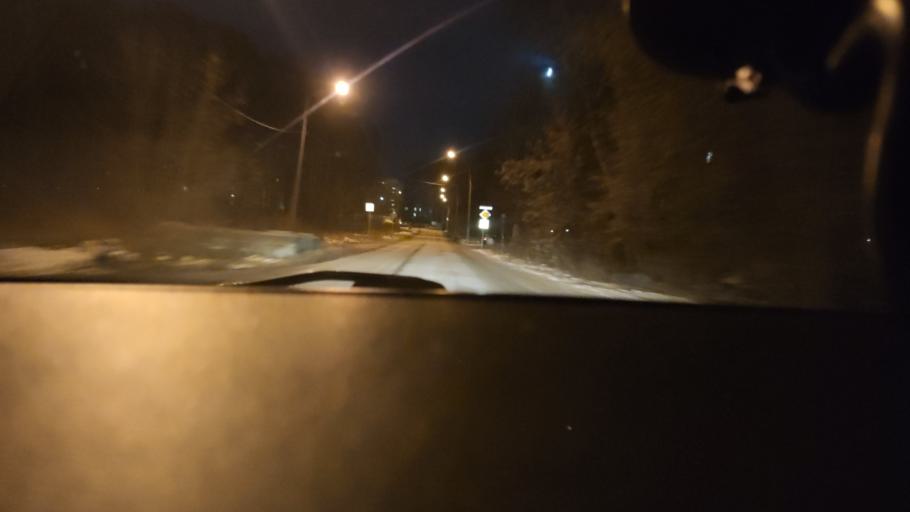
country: RU
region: Perm
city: Kondratovo
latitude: 58.0295
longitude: 56.0112
